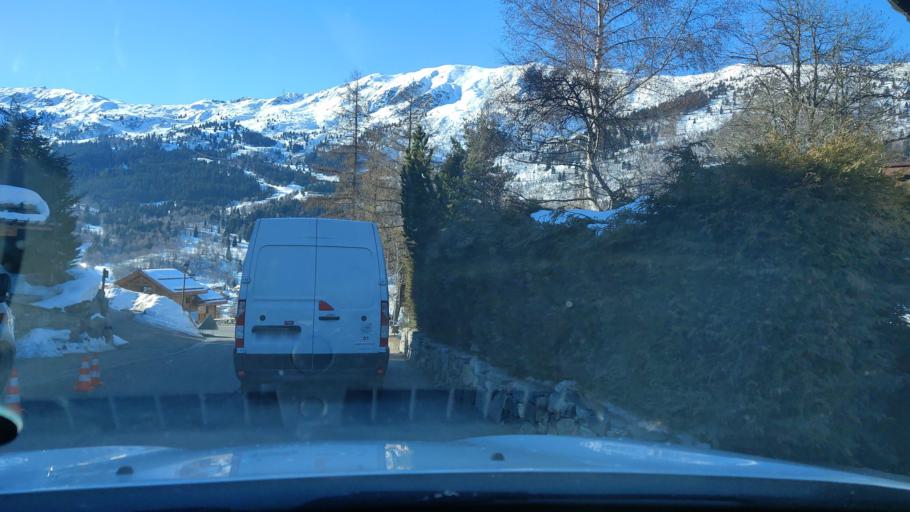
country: FR
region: Rhone-Alpes
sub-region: Departement de la Savoie
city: Meribel
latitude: 45.4151
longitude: 6.5636
